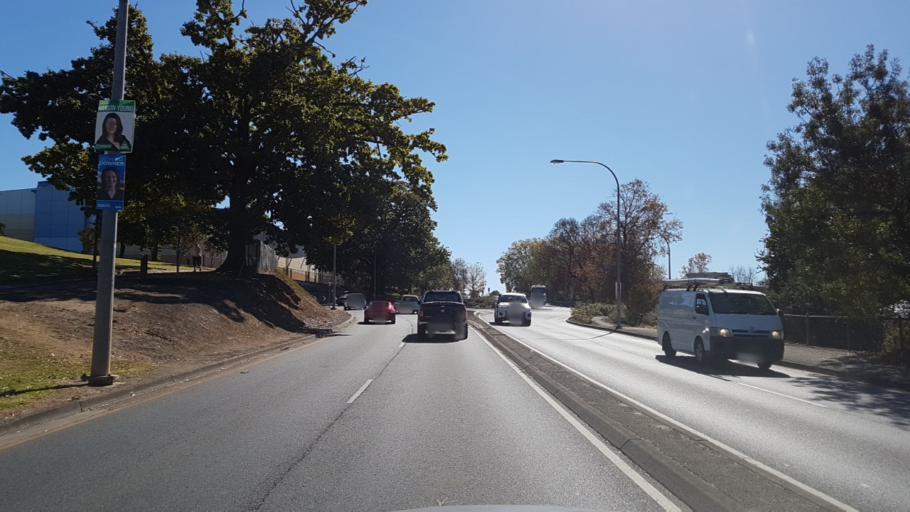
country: AU
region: South Australia
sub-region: Mount Barker
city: Mount Barker
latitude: -35.0698
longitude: 138.8571
